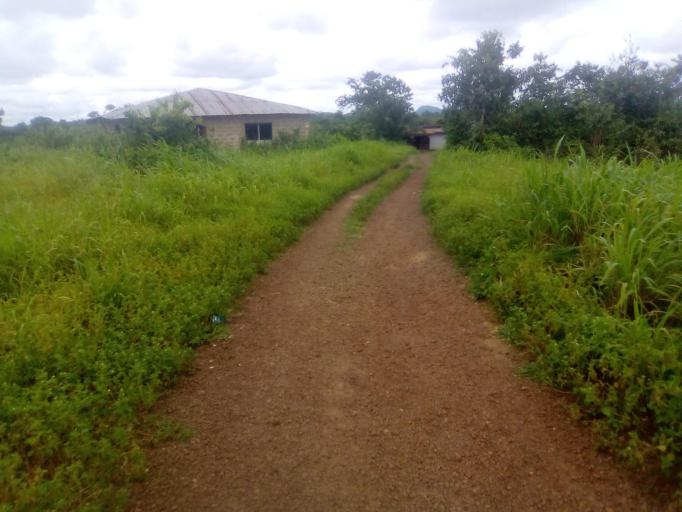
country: SL
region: Southern Province
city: Moyamba
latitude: 8.1464
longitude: -12.4336
